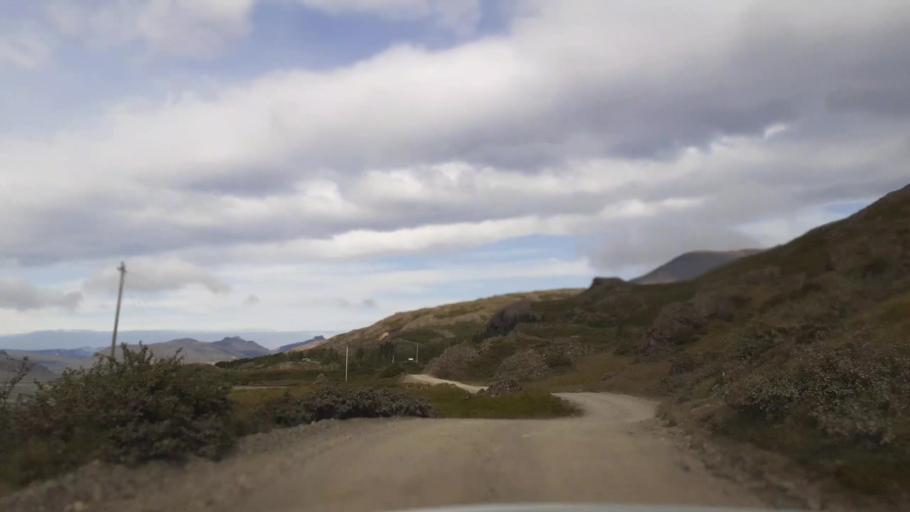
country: IS
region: East
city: Hoefn
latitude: 64.4328
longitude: -14.8923
